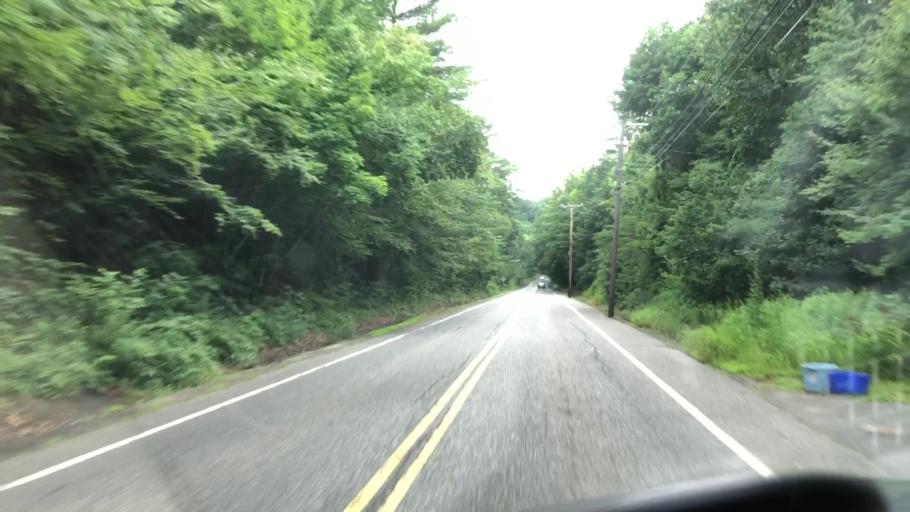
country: US
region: Massachusetts
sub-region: Hampshire County
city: Easthampton
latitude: 42.2134
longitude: -72.6721
